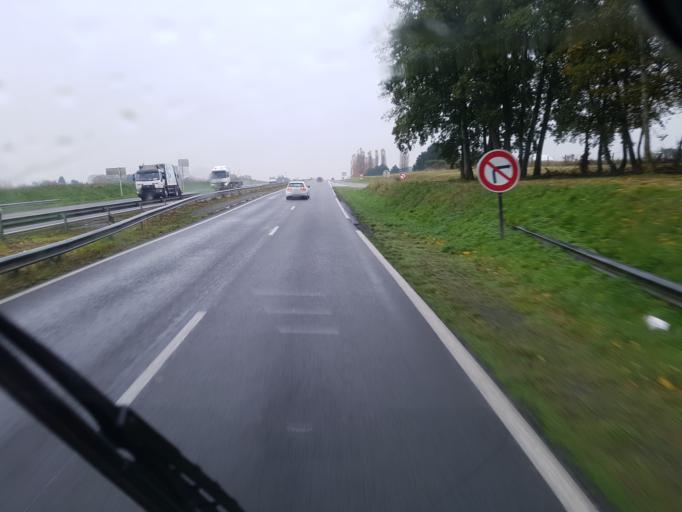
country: FR
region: Picardie
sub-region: Departement de l'Aisne
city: Gauchy
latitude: 49.8148
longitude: 3.2904
